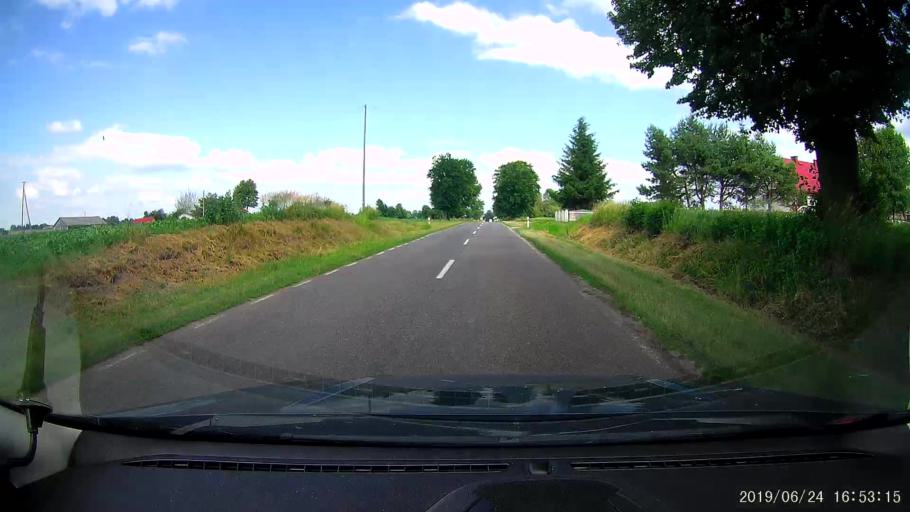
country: PL
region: Lublin Voivodeship
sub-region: Powiat tomaszowski
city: Telatyn
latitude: 50.5355
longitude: 23.7969
